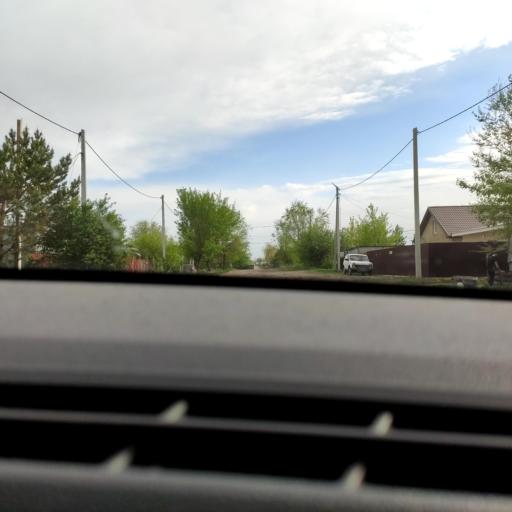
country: RU
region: Samara
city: Tol'yatti
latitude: 53.5557
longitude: 49.4087
